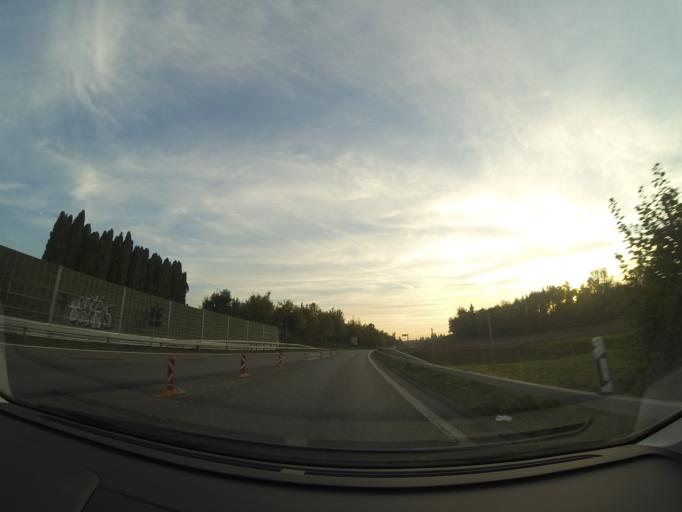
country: CH
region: Zurich
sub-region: Bezirk Hinwil
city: Hinwil
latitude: 47.2996
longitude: 8.8334
